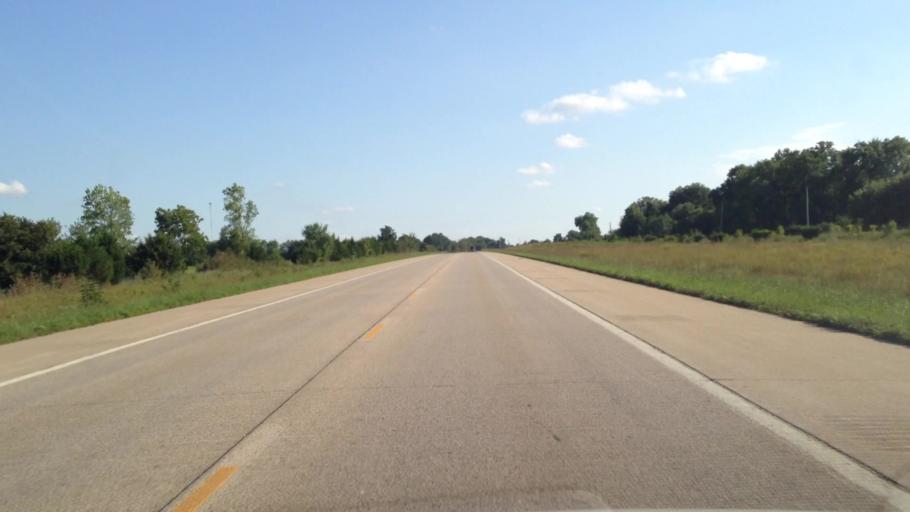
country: US
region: Kansas
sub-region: Crawford County
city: Arma
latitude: 37.5642
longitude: -94.7047
